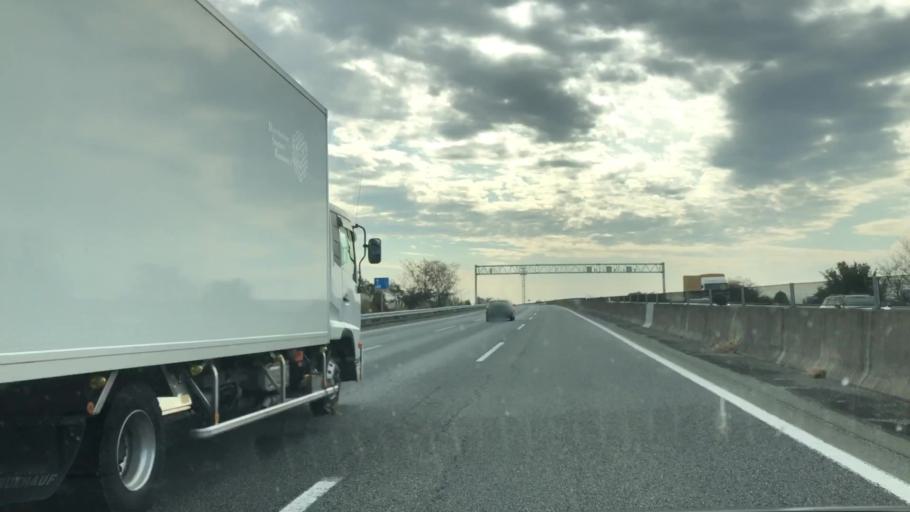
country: JP
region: Saga Prefecture
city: Tosu
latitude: 33.3578
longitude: 130.5393
